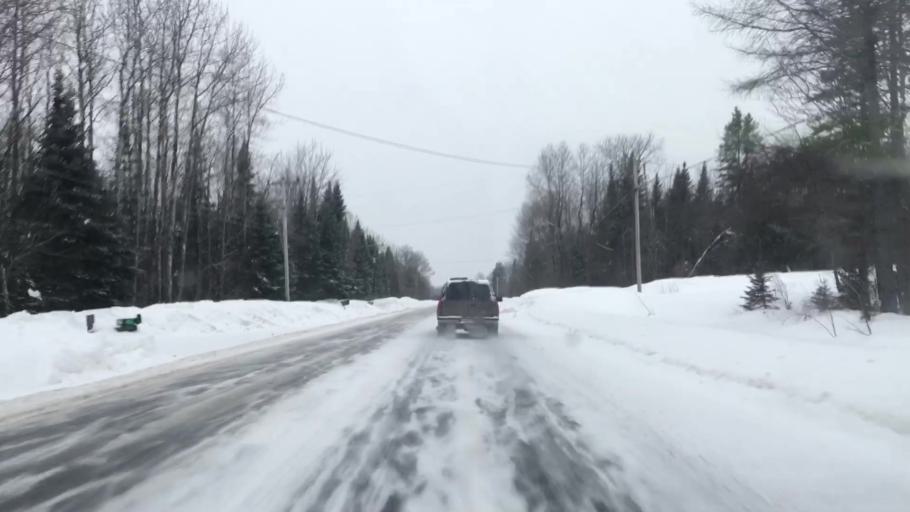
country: US
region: Maine
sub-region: Penobscot County
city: Medway
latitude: 45.5871
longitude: -68.4357
